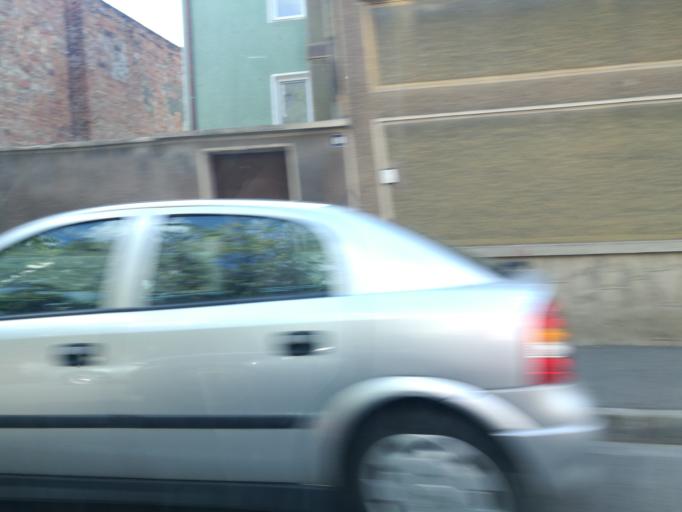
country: RO
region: Bihor
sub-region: Comuna Biharea
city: Oradea
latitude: 47.0551
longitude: 21.9198
